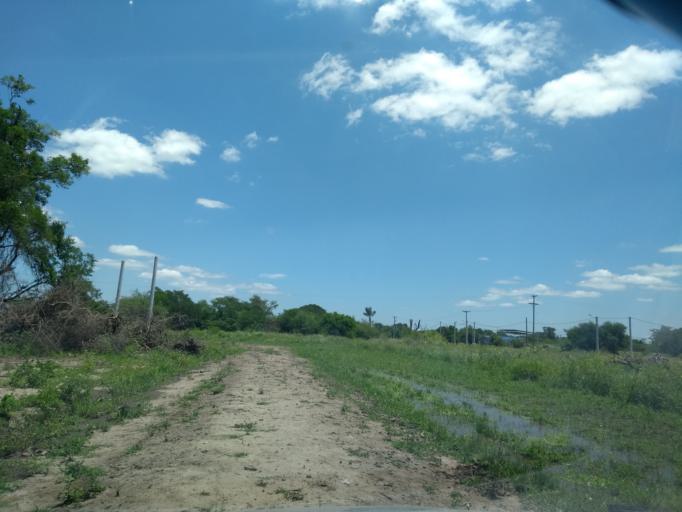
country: AR
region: Chaco
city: Fontana
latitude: -27.4025
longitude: -58.9742
